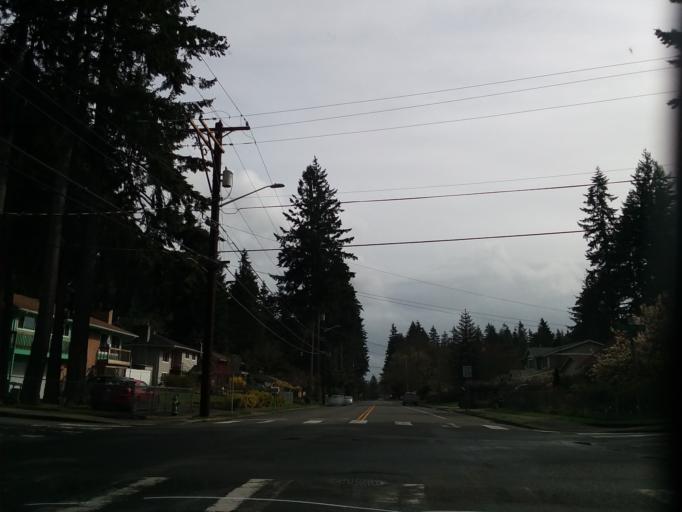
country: US
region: Washington
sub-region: Snohomish County
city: Mountlake Terrace
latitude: 47.7923
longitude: -122.3220
